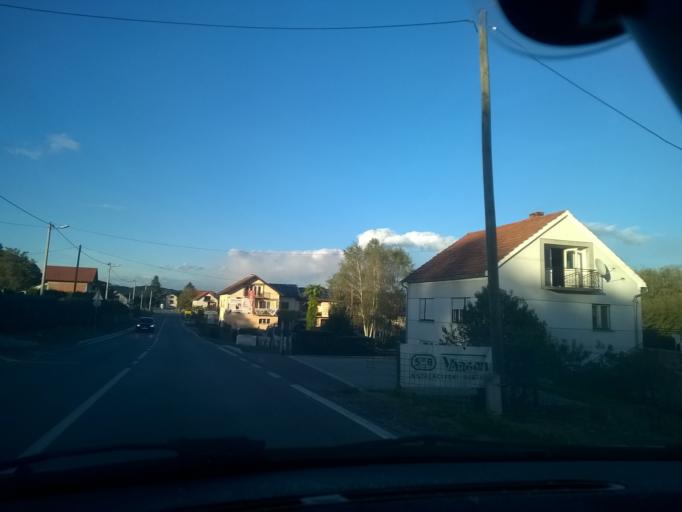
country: HR
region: Zagrebacka
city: Jakovlje
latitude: 46.0069
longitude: 15.8520
